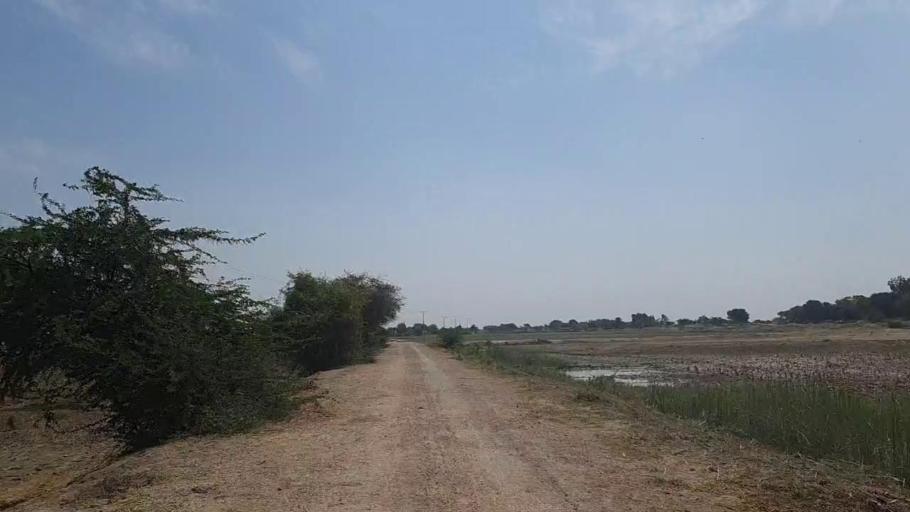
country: PK
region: Sindh
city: Mirpur Batoro
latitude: 24.6700
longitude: 68.2914
